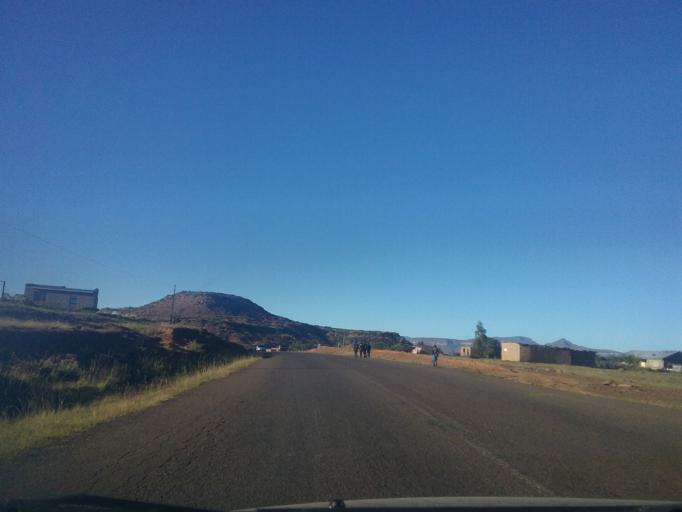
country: LS
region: Quthing
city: Quthing
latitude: -30.3325
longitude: 27.5334
